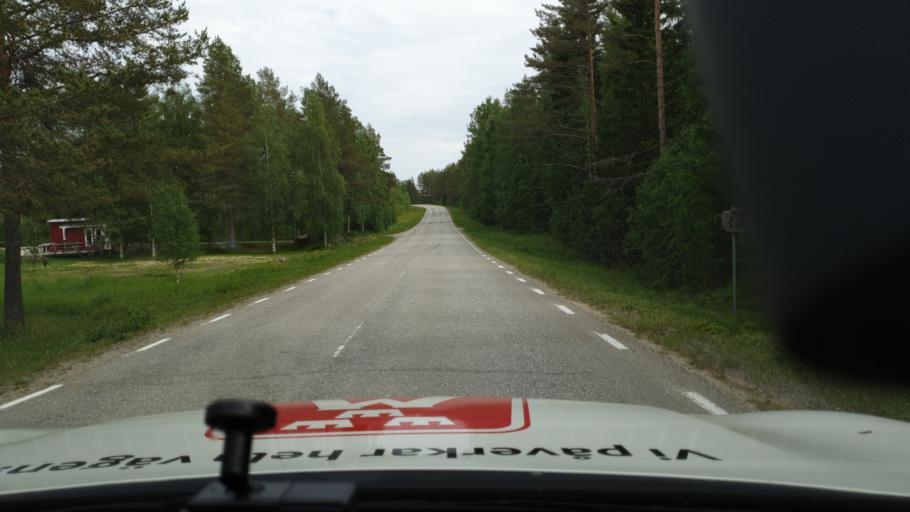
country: SE
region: Vaesterbotten
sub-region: Umea Kommun
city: Hoernefors
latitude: 63.5664
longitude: 19.8058
